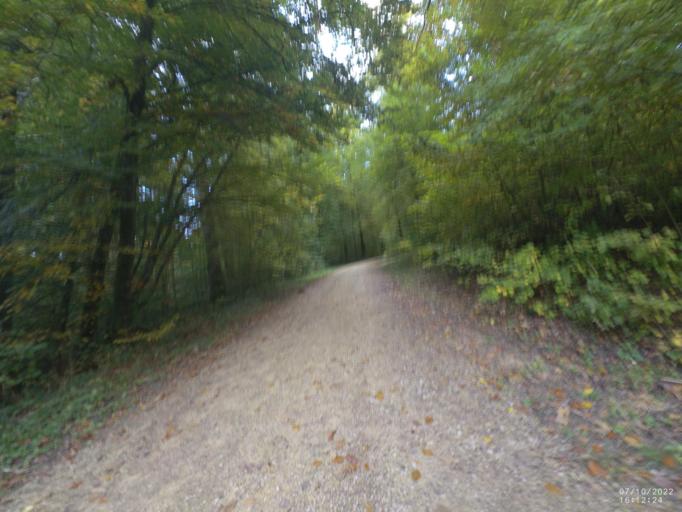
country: DE
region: Baden-Wuerttemberg
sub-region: Regierungsbezirk Stuttgart
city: Eislingen
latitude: 48.7173
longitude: 9.7159
